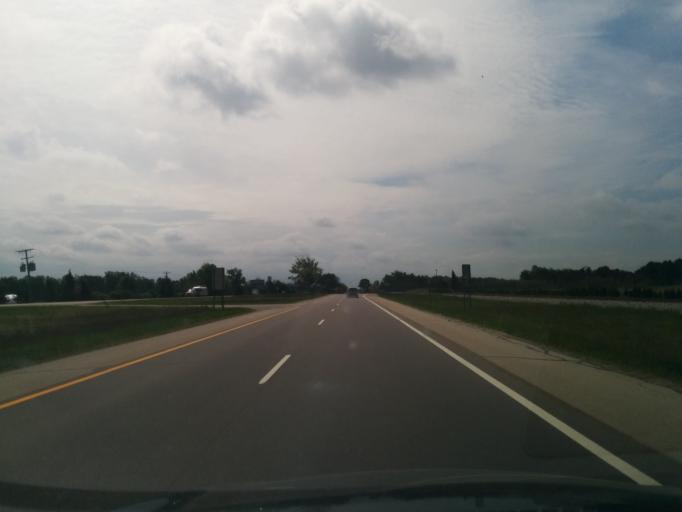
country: US
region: Michigan
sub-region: Ottawa County
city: Grand Haven
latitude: 42.9462
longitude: -86.1641
